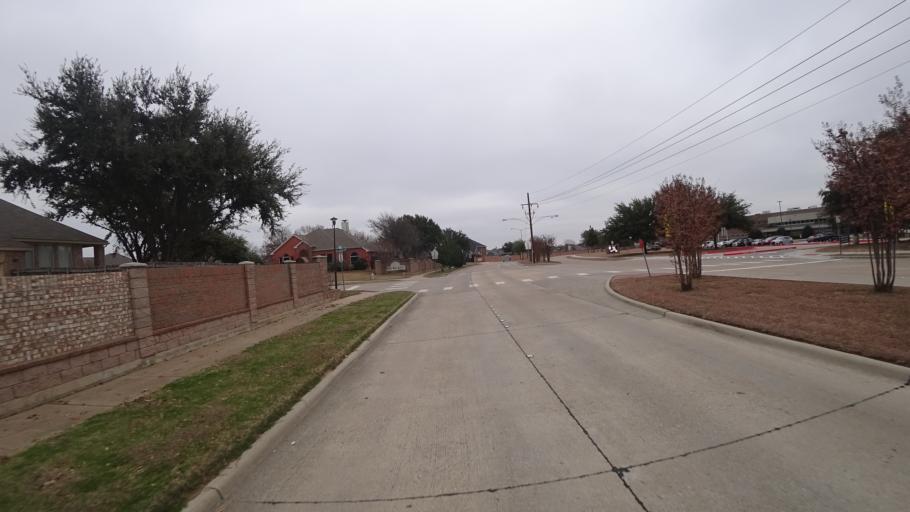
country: US
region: Texas
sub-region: Denton County
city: Highland Village
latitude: 33.0569
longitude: -97.0327
